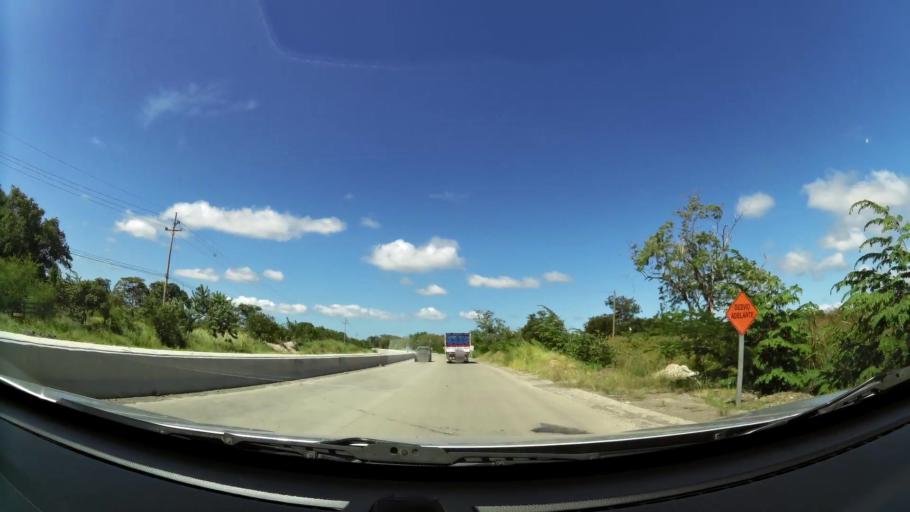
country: CR
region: Guanacaste
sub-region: Canton de Canas
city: Canas
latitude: 10.4565
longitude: -85.1327
